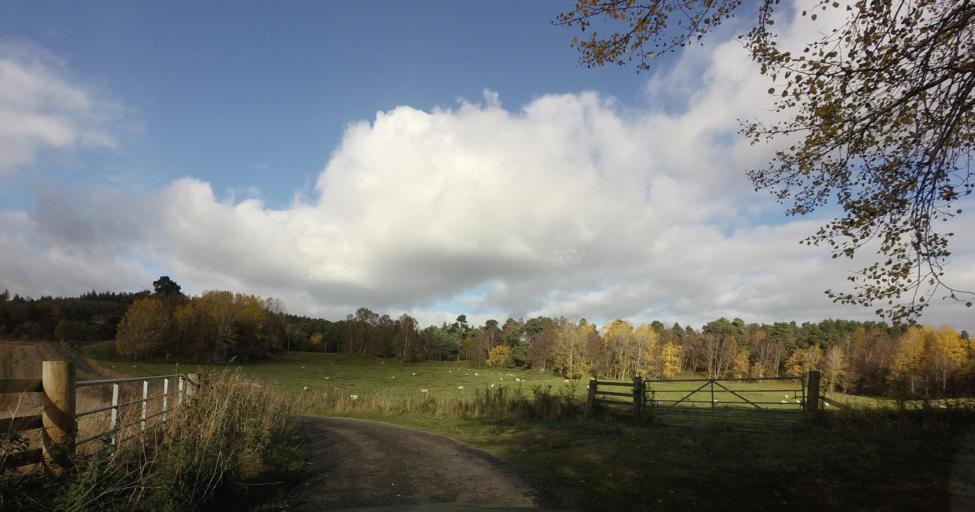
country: GB
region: Scotland
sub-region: Highland
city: Grantown on Spey
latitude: 57.3178
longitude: -3.6179
